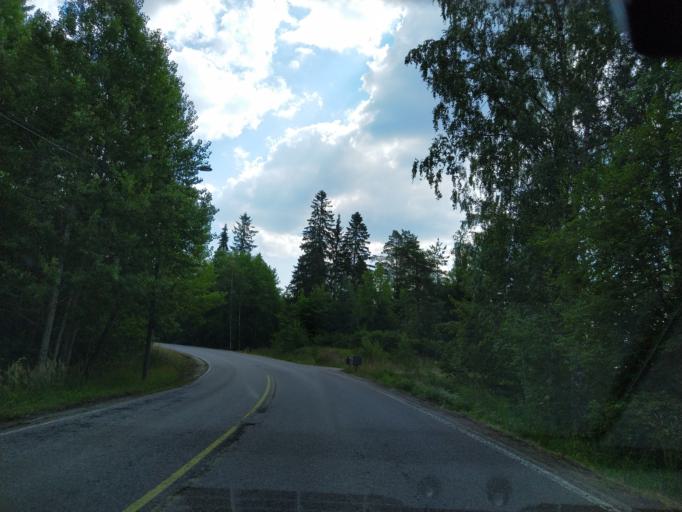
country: FI
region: Uusimaa
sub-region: Helsinki
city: Kirkkonummi
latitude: 60.1048
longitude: 24.4801
